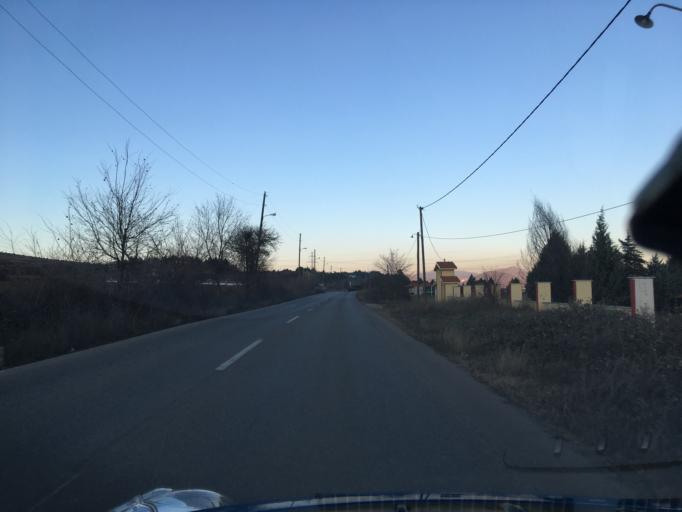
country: GR
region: West Macedonia
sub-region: Nomos Kozanis
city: Kozani
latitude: 40.2582
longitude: 21.7593
